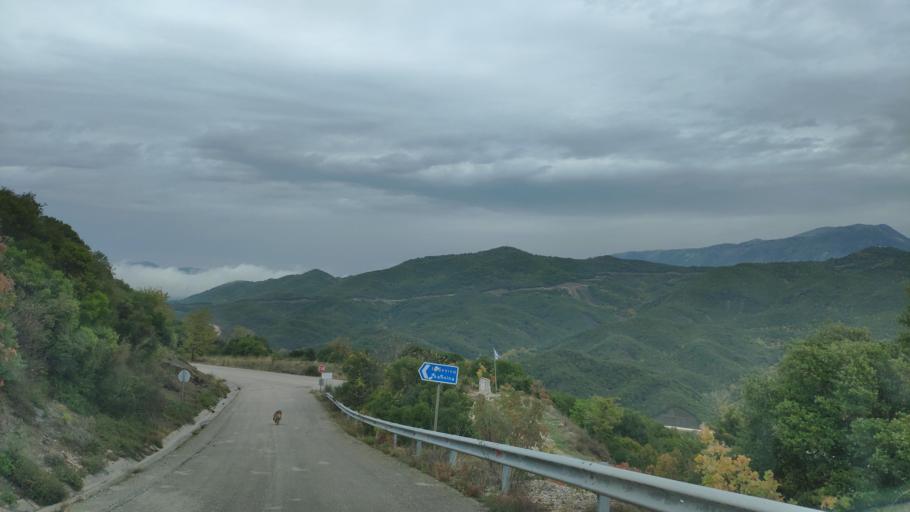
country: GR
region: Epirus
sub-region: Nomos Thesprotias
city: Paramythia
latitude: 39.4579
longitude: 20.6786
